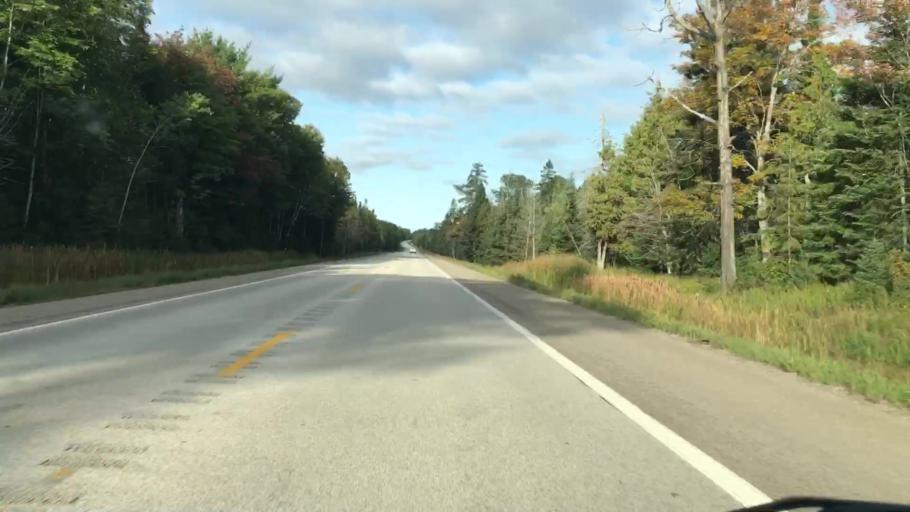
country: US
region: Michigan
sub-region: Luce County
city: Newberry
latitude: 46.3319
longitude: -85.0648
